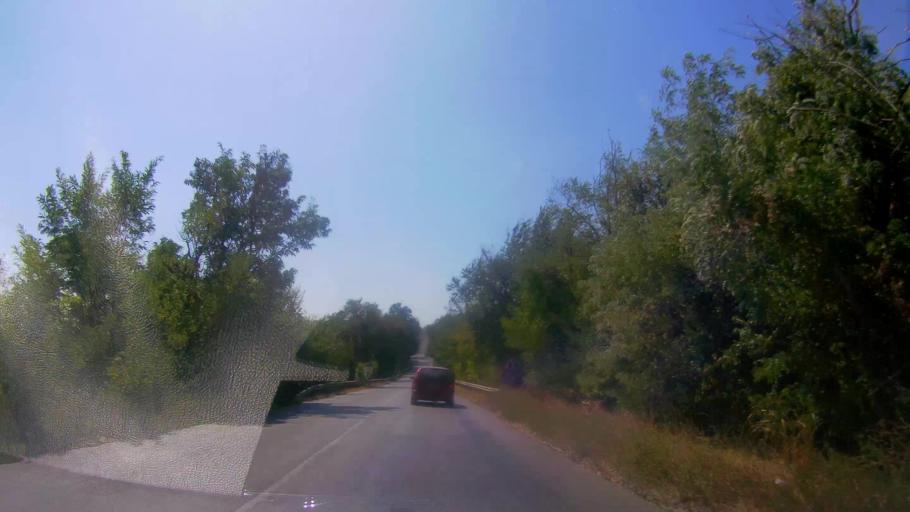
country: BG
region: Veliko Turnovo
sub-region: Obshtina Gorna Oryakhovitsa
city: Purvomaytsi
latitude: 43.2431
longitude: 25.6431
